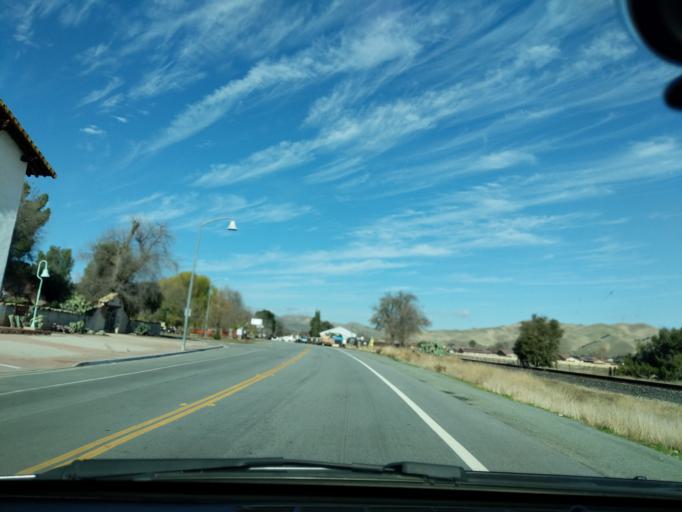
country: US
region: California
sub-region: San Luis Obispo County
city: San Miguel
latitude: 35.7447
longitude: -120.6970
